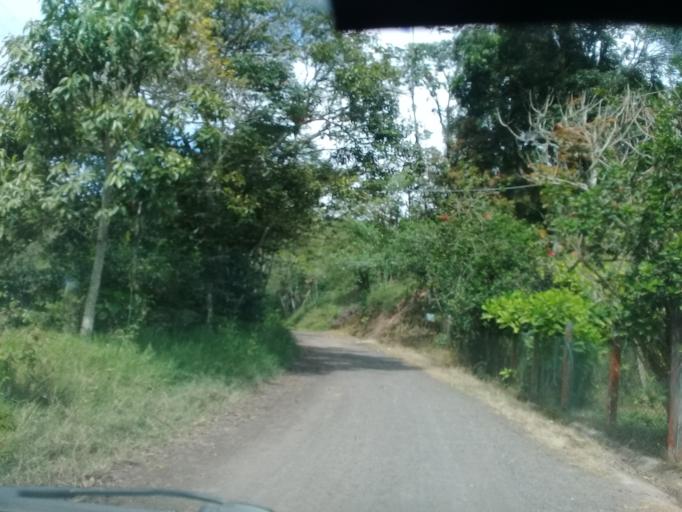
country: CO
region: Cundinamarca
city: Granada
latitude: 5.0980
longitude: -74.5640
